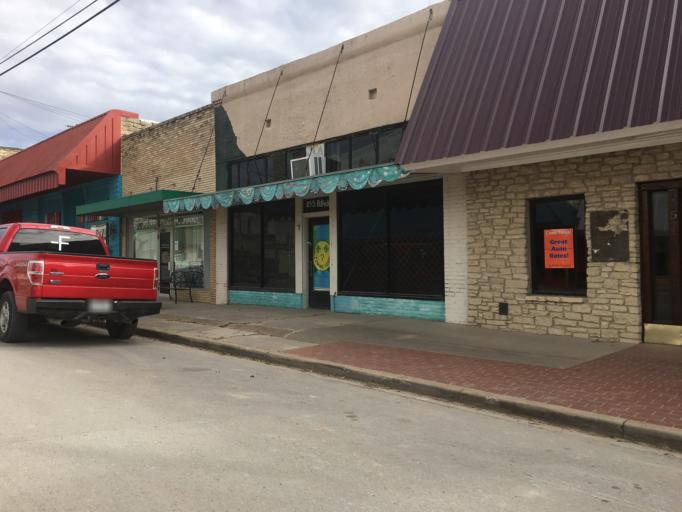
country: US
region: Texas
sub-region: Erath County
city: Dublin
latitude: 32.0846
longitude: -98.3425
